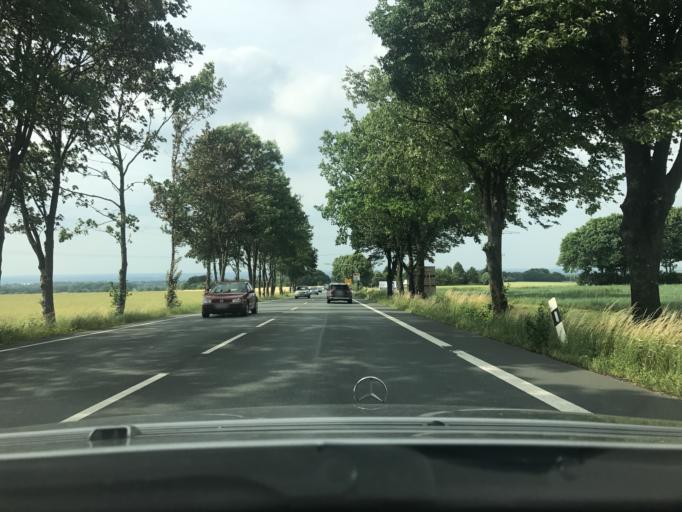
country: DE
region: North Rhine-Westphalia
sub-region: Regierungsbezirk Arnsberg
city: Unna
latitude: 51.5020
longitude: 7.7029
